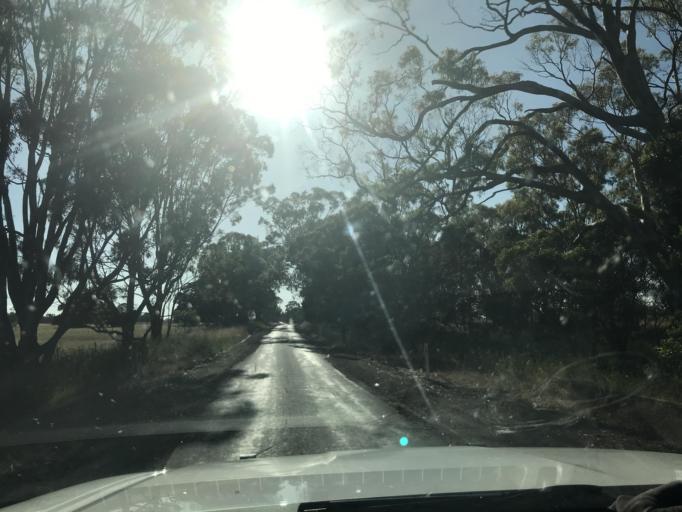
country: AU
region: Victoria
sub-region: Horsham
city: Horsham
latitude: -37.0042
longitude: 141.6126
